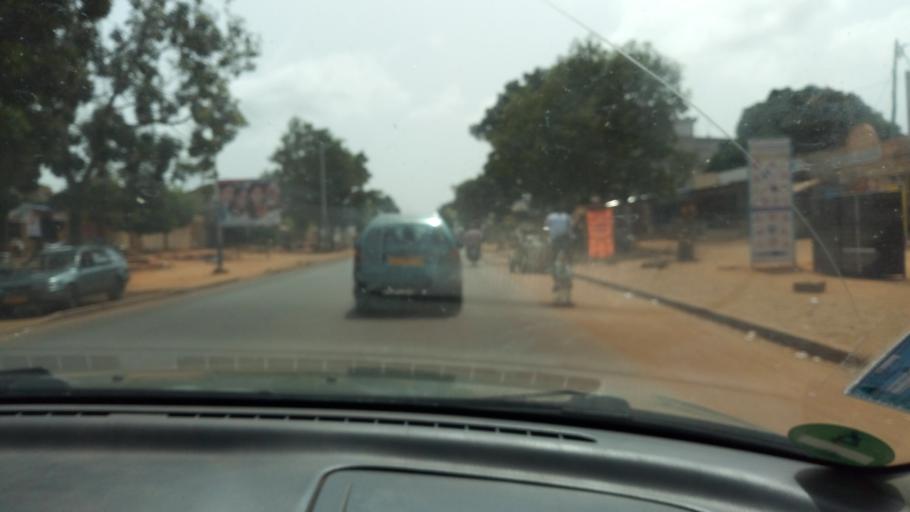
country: TG
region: Maritime
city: Lome
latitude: 6.1768
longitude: 1.1788
